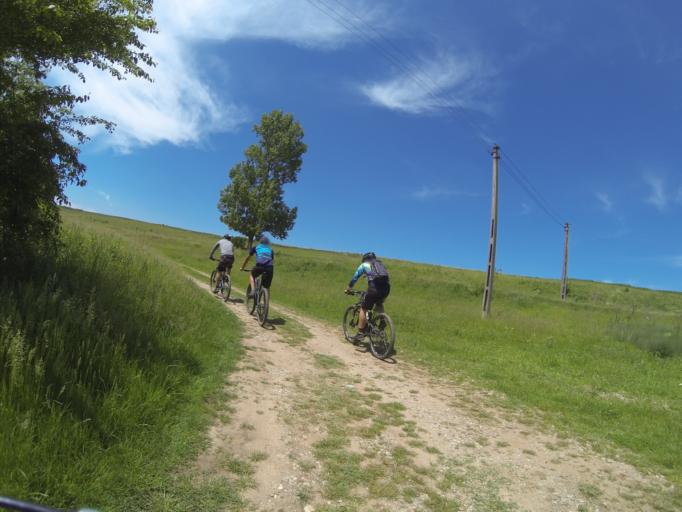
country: RO
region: Dolj
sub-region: Comuna Teslui
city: Teslui
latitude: 44.2011
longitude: 24.1425
